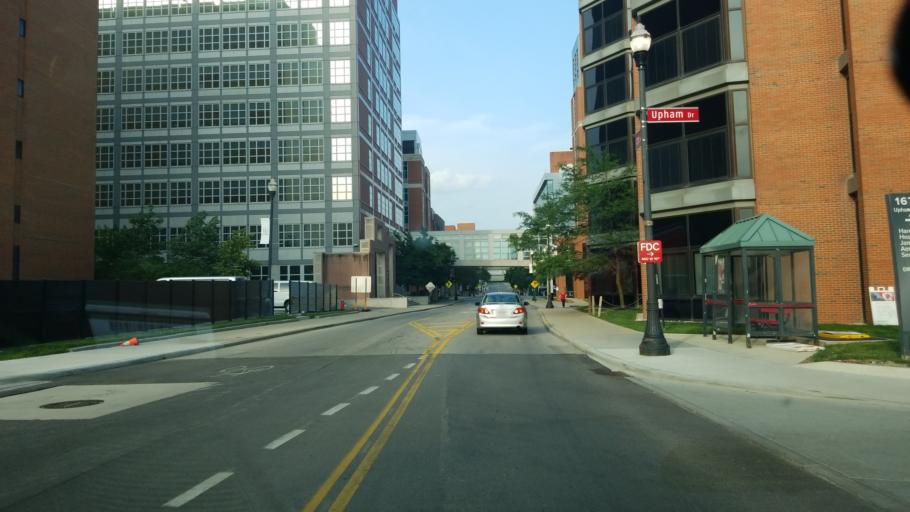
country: US
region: Ohio
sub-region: Franklin County
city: Grandview Heights
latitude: 39.9960
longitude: -83.0205
